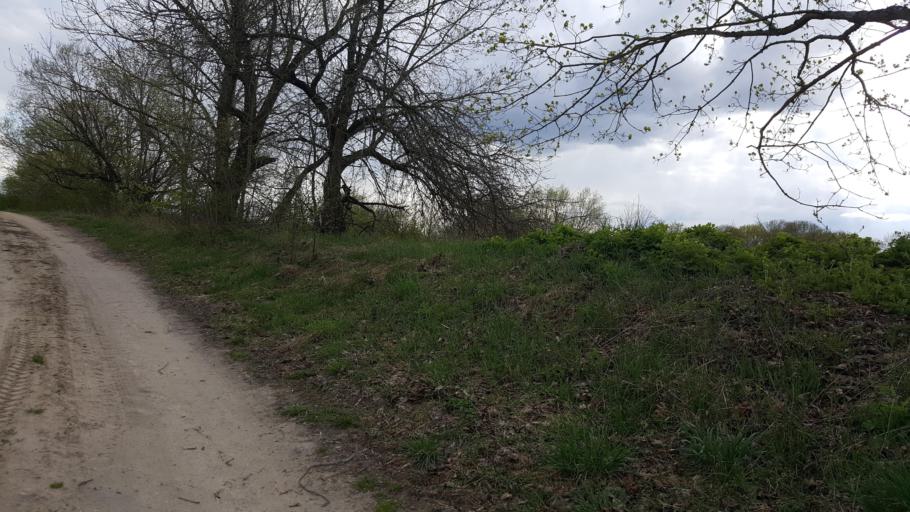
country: BY
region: Brest
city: Kamyanyets
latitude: 52.4065
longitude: 23.7093
